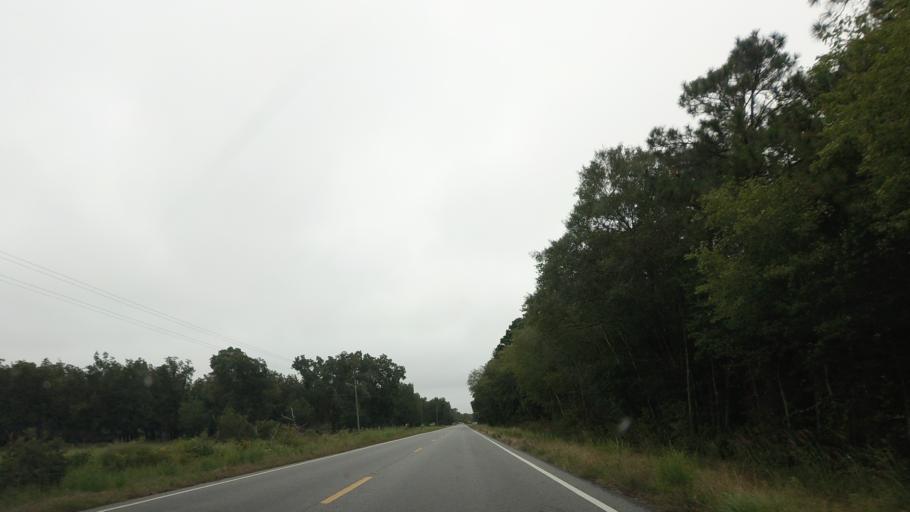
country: US
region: Georgia
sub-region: Berrien County
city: Enigma
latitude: 31.3686
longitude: -83.2266
